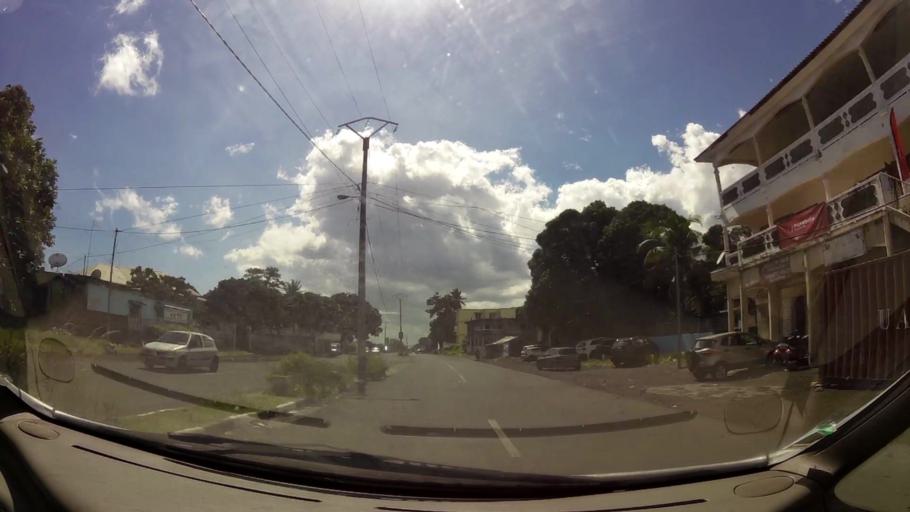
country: KM
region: Grande Comore
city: Mavingouni
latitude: -11.7137
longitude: 43.2461
